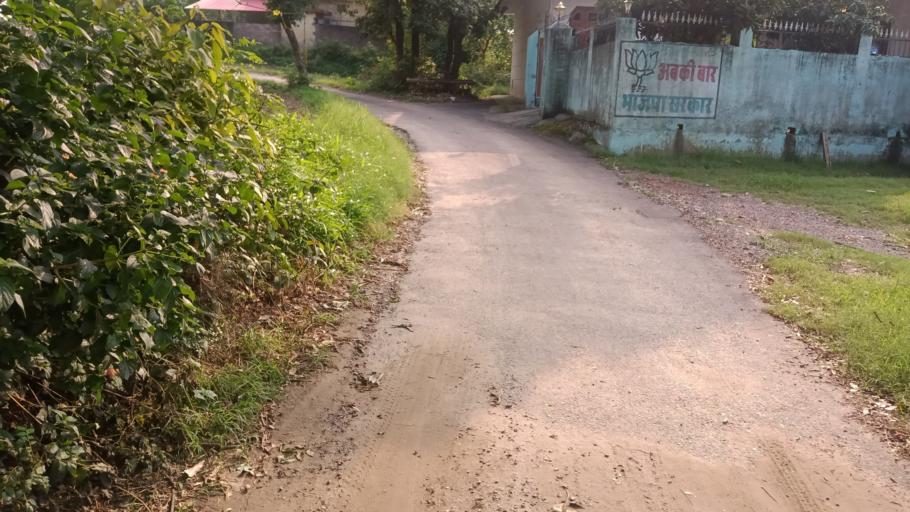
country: IN
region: Himachal Pradesh
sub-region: Hamirpur
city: Nadaun
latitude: 31.6914
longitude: 76.3555
